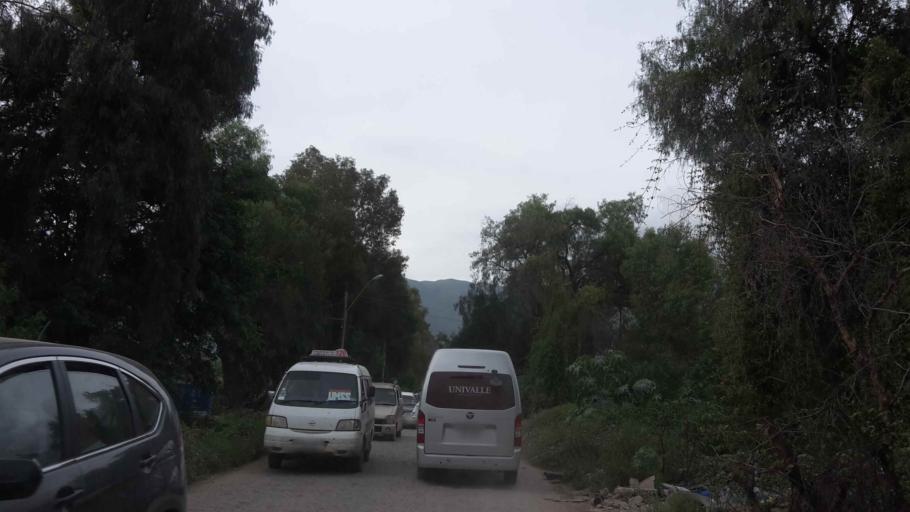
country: BO
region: Cochabamba
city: Cochabamba
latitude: -17.3736
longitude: -66.2074
